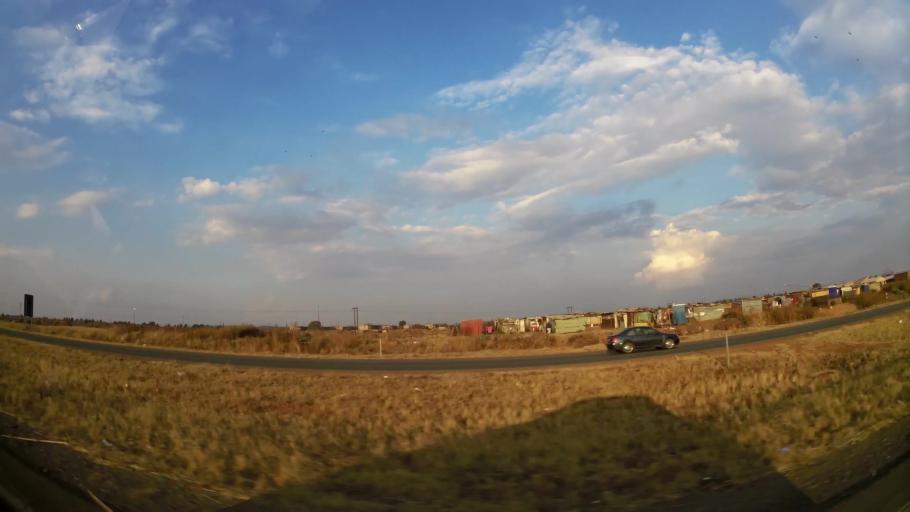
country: ZA
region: Gauteng
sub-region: Sedibeng District Municipality
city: Vanderbijlpark
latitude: -26.5982
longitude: 27.8193
